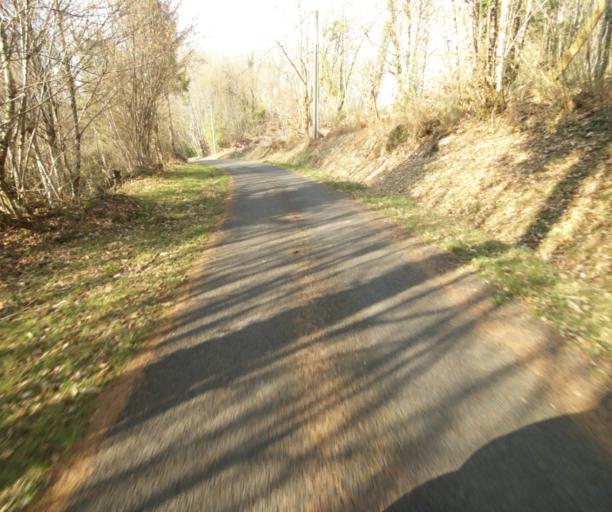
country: FR
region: Limousin
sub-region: Departement de la Correze
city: Saint-Clement
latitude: 45.3433
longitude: 1.6529
